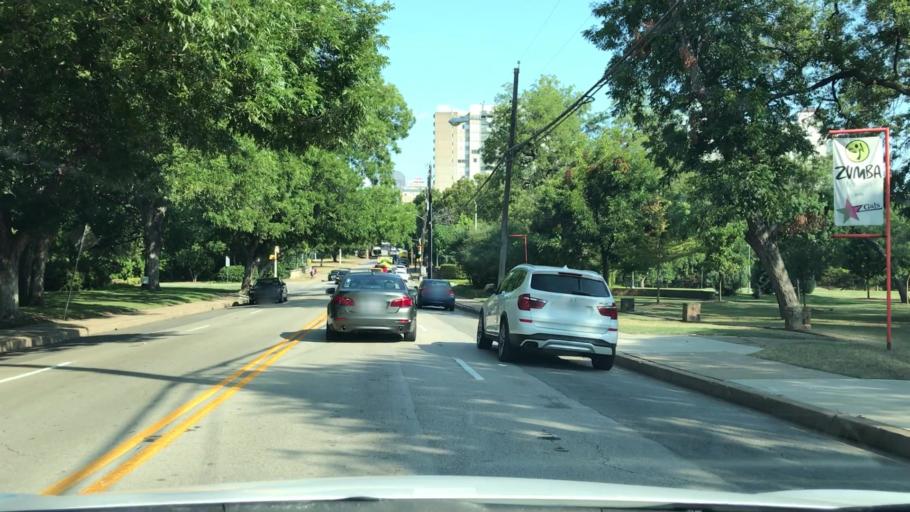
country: US
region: Texas
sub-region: Dallas County
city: Dallas
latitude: 32.8020
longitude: -96.8118
